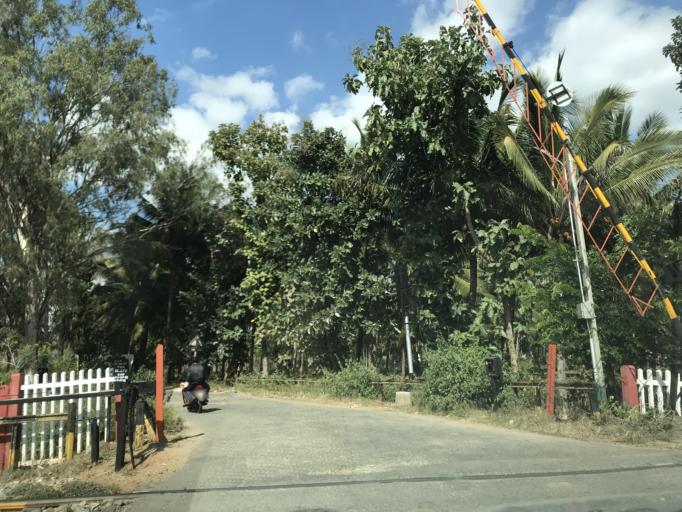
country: IN
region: Karnataka
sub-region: Mandya
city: Krishnarajpet
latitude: 12.7292
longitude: 76.3814
